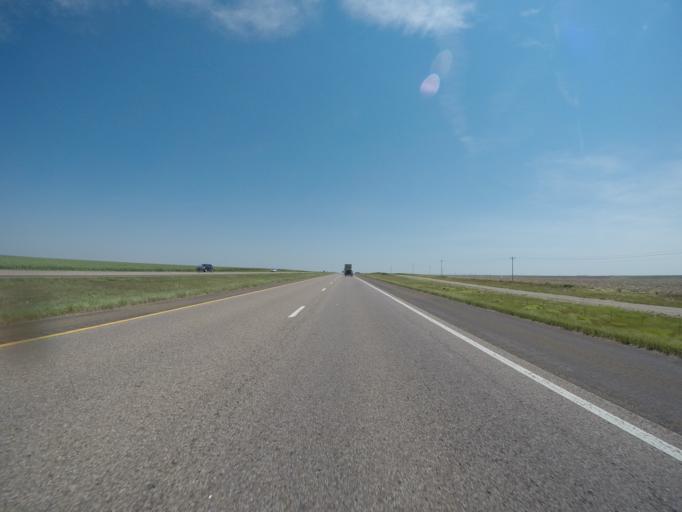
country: US
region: Kansas
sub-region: Thomas County
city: Colby
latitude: 39.3515
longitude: -101.3469
